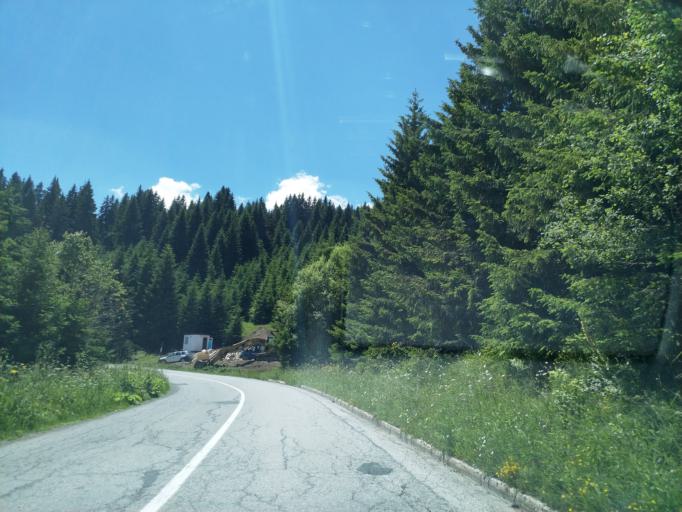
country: XK
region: Mitrovica
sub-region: Komuna e Leposaviqit
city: Leposaviq
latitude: 43.3232
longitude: 20.8446
